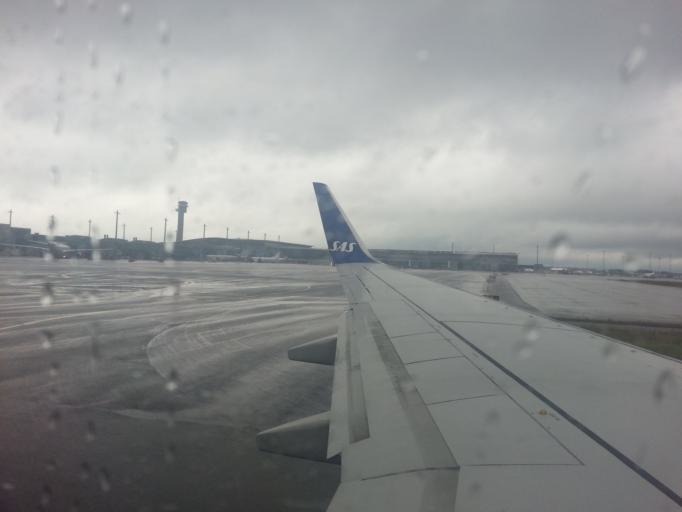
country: NO
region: Akershus
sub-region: Ullensaker
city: Jessheim
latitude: 60.1951
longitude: 11.1134
